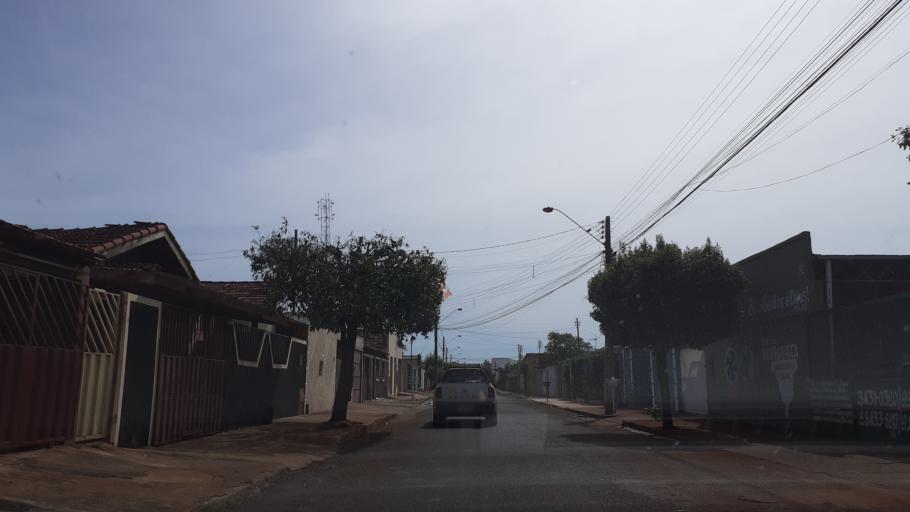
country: BR
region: Goias
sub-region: Itumbiara
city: Itumbiara
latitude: -18.4123
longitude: -49.2295
